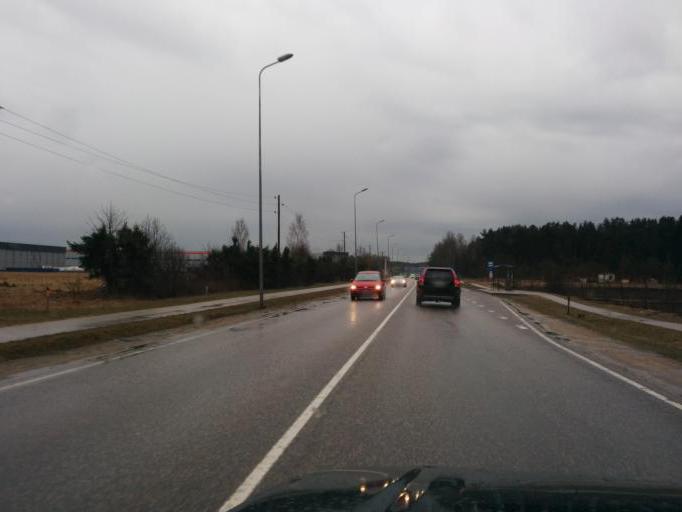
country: LV
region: Kekava
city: Balozi
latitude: 56.8963
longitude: 24.1474
